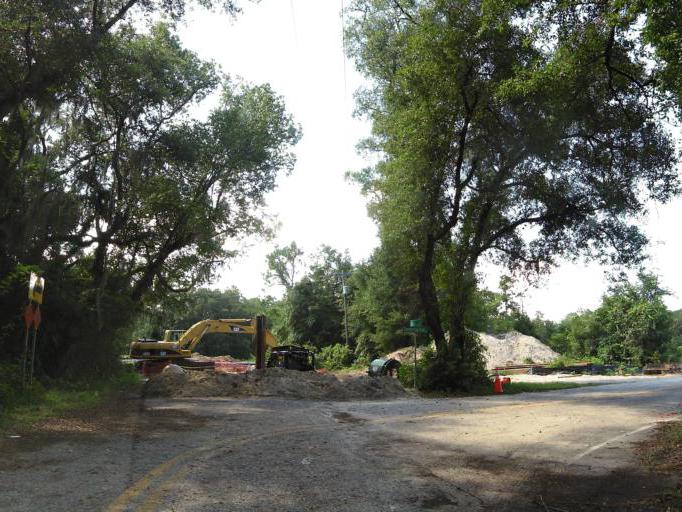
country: US
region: Florida
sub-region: Nassau County
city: Yulee
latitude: 30.6027
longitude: -81.6015
